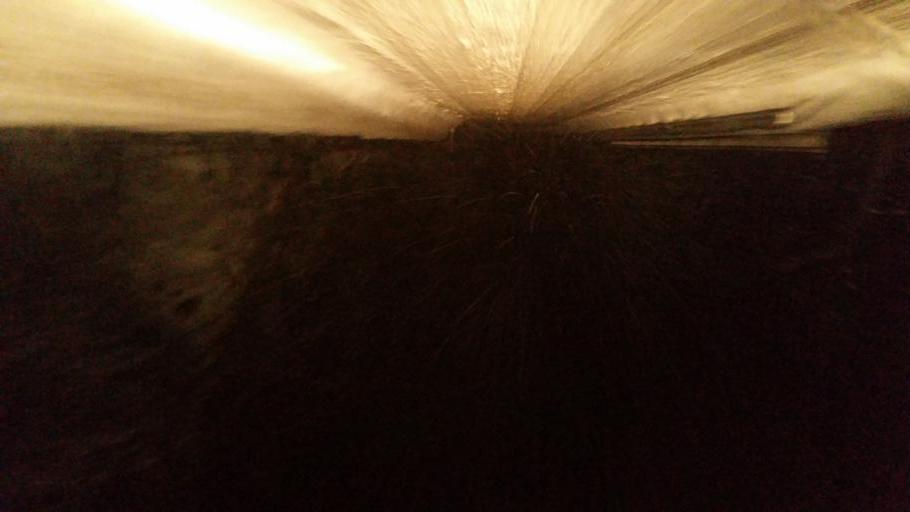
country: AT
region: Salzburg
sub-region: Politischer Bezirk Hallein
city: Abtenau
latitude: 47.5038
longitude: 13.4247
